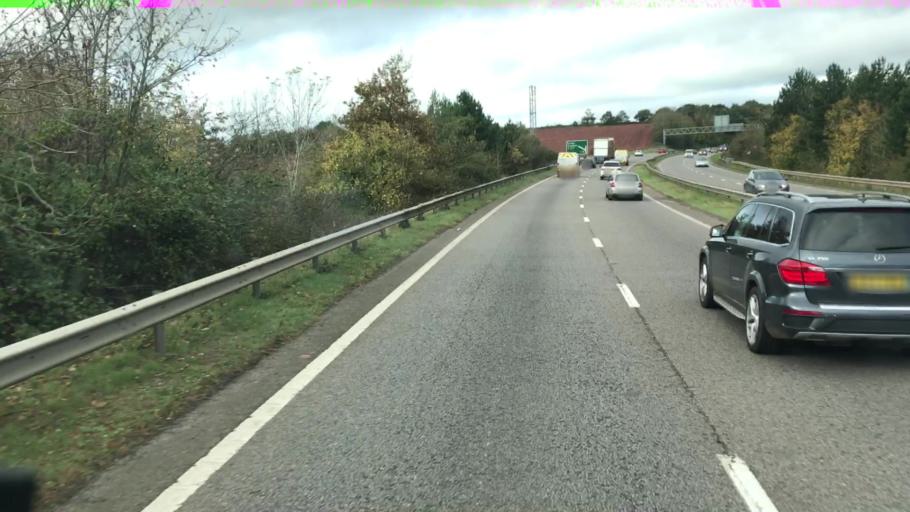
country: GB
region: England
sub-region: Devon
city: Exeter
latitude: 50.6892
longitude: -3.5345
